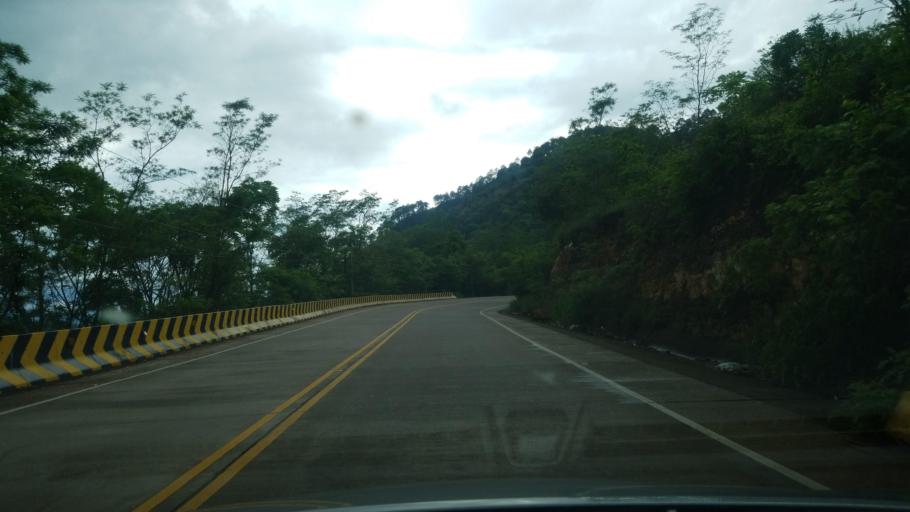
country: HN
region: Copan
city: Copan
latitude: 14.8400
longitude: -89.1775
